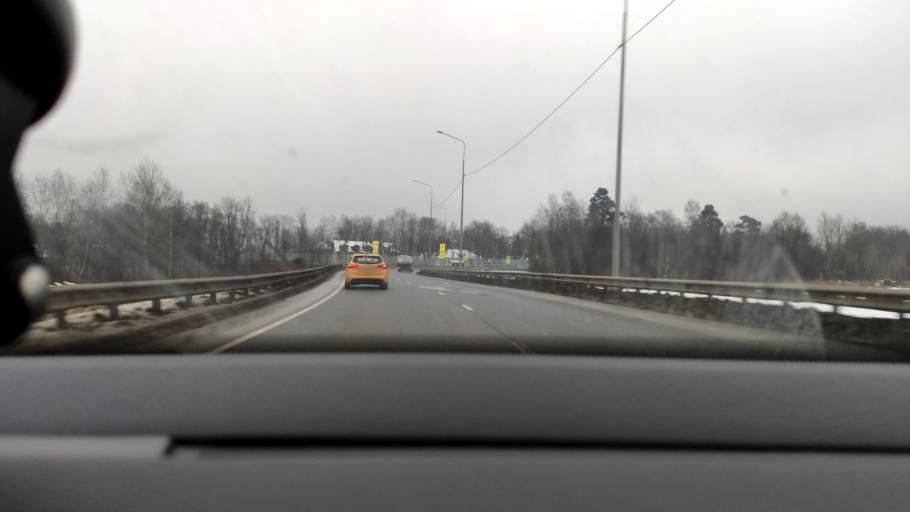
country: RU
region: Moskovskaya
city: Sergiyev Posad
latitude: 56.2720
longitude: 38.1179
